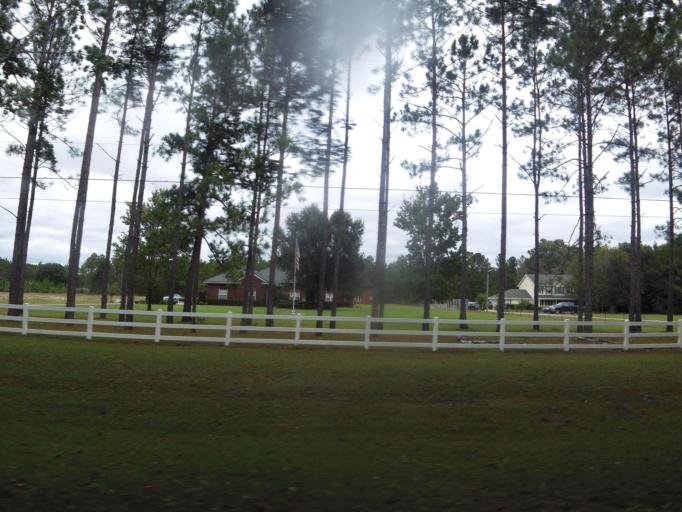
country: US
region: Florida
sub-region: Clay County
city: Lakeside
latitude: 30.2029
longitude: -81.8580
